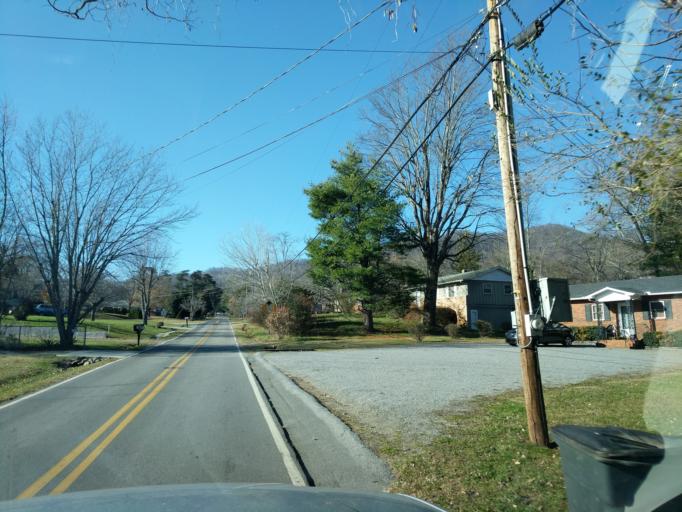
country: US
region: North Carolina
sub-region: Buncombe County
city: Swannanoa
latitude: 35.6063
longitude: -82.3826
